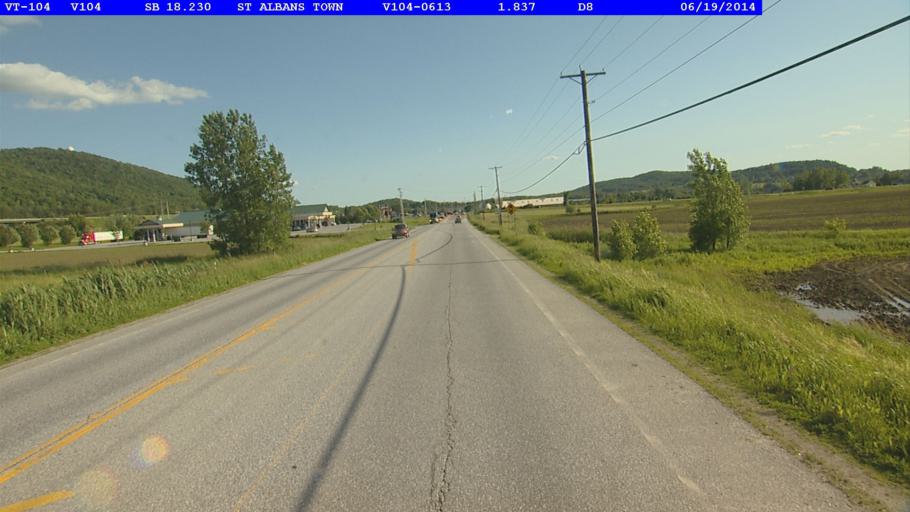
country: US
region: Vermont
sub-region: Franklin County
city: Saint Albans
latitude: 44.7993
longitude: -73.0718
